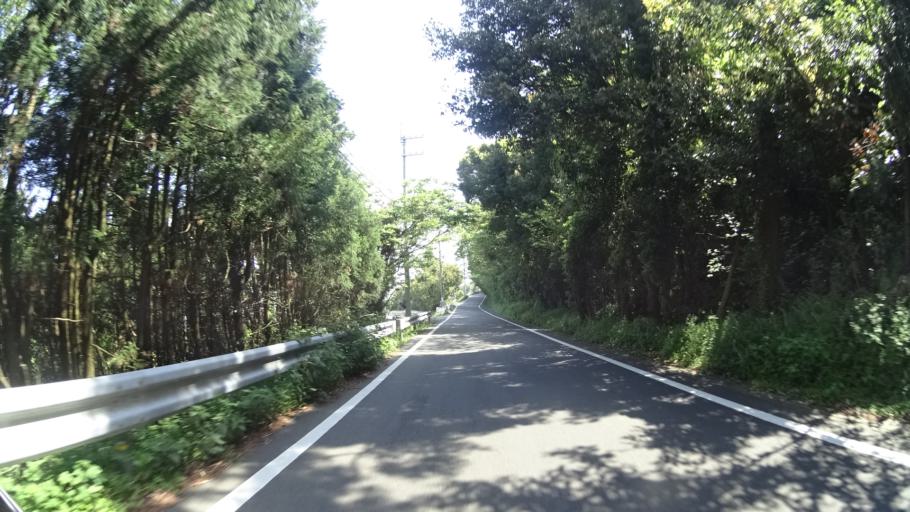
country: JP
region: Ehime
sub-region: Nishiuwa-gun
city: Ikata-cho
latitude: 33.3785
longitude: 132.0657
